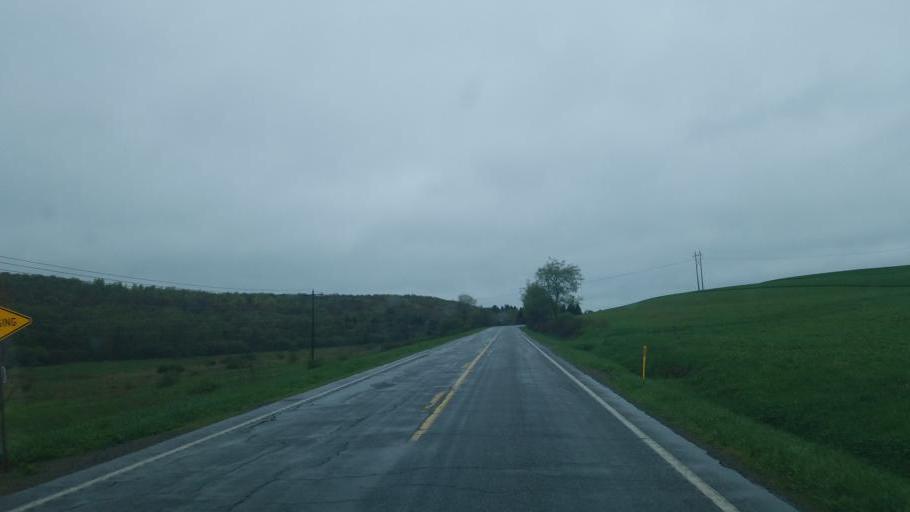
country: US
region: Pennsylvania
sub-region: Potter County
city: Coudersport
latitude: 41.8661
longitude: -77.8458
